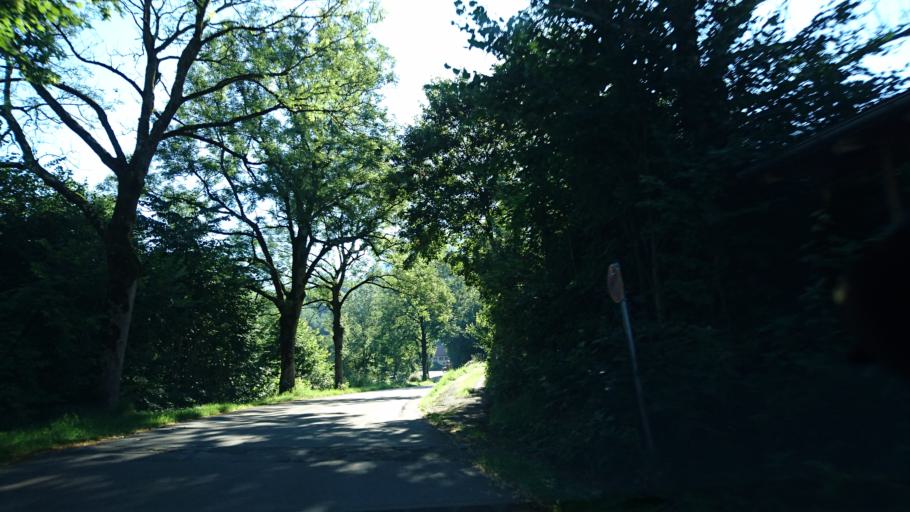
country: DE
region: Bavaria
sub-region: Swabia
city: Halblech
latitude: 47.6250
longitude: 10.8192
